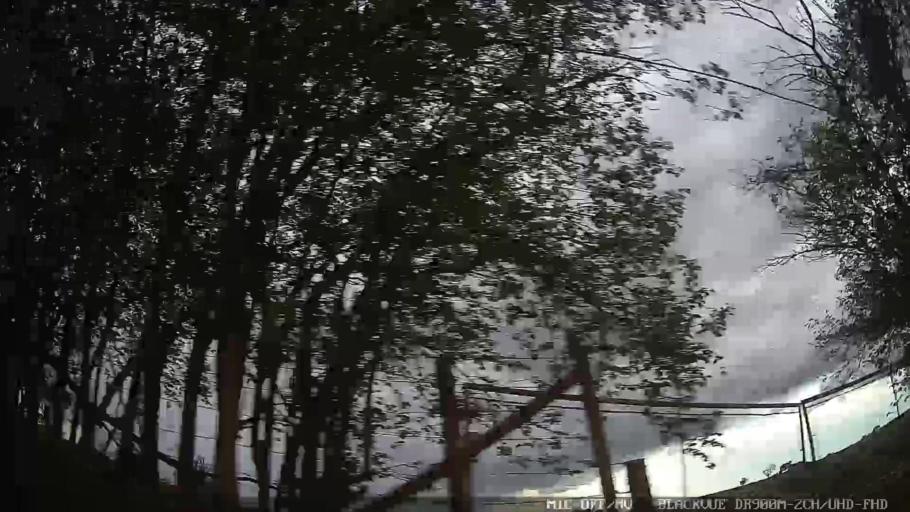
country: BR
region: Sao Paulo
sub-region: Jaguariuna
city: Jaguariuna
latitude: -22.7574
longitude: -47.0051
